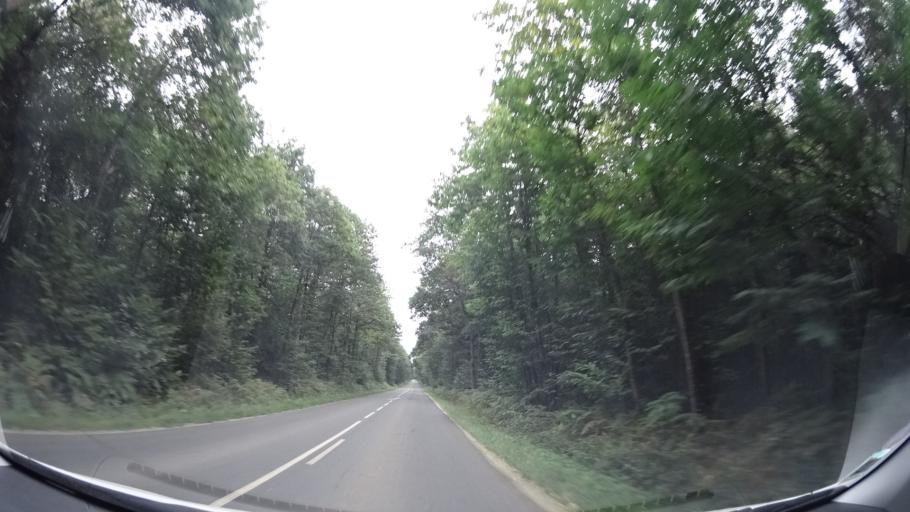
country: FR
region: Brittany
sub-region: Departement d'Ille-et-Vilaine
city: Pleugueneuc
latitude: 48.3524
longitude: -1.9231
